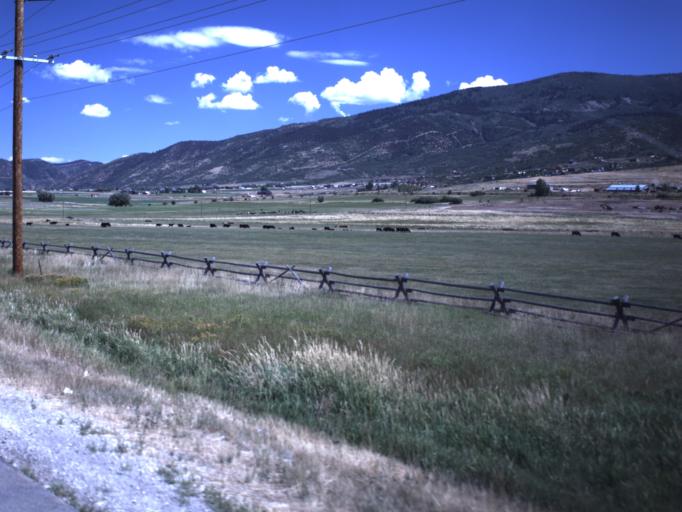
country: US
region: Utah
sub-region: Summit County
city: Kamas
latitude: 40.6614
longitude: -111.2808
